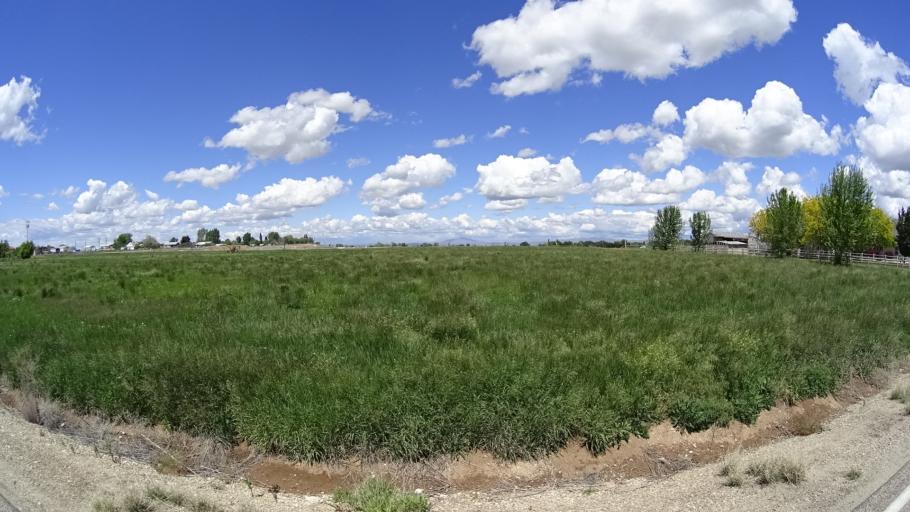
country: US
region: Idaho
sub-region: Ada County
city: Meridian
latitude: 43.5830
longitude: -116.4504
